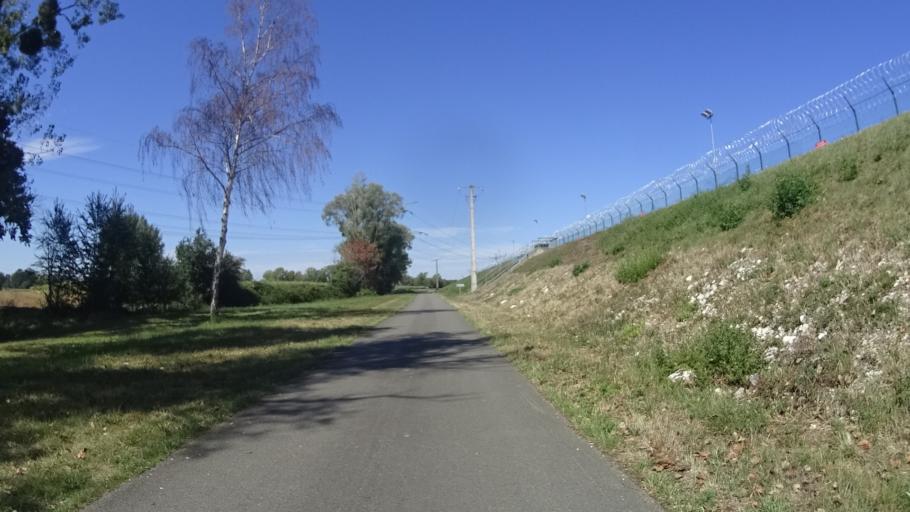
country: FR
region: Bourgogne
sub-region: Departement de la Nievre
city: Neuvy-sur-Loire
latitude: 47.5029
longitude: 2.8783
